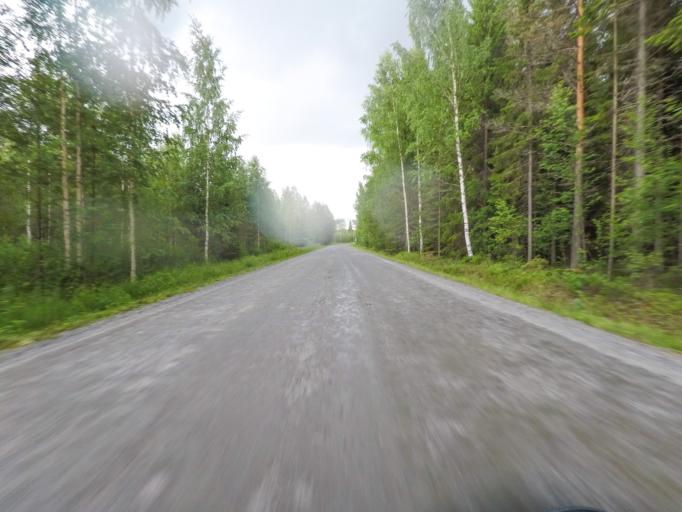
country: FI
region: Central Finland
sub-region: Jyvaeskylae
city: Hankasalmi
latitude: 62.3891
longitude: 26.6031
